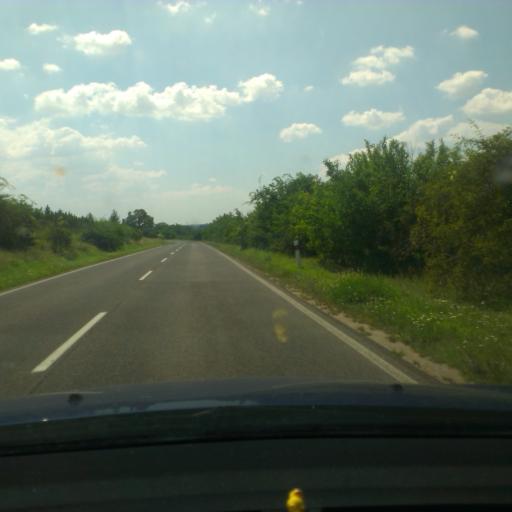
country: SK
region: Trnavsky
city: Hlohovec
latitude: 48.4553
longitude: 17.8125
